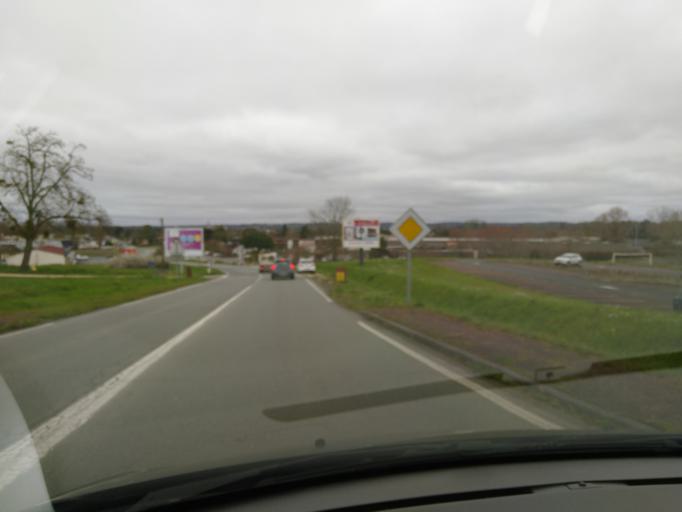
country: FR
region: Aquitaine
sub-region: Departement de la Dordogne
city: Bergerac
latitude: 44.8281
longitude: 0.5016
